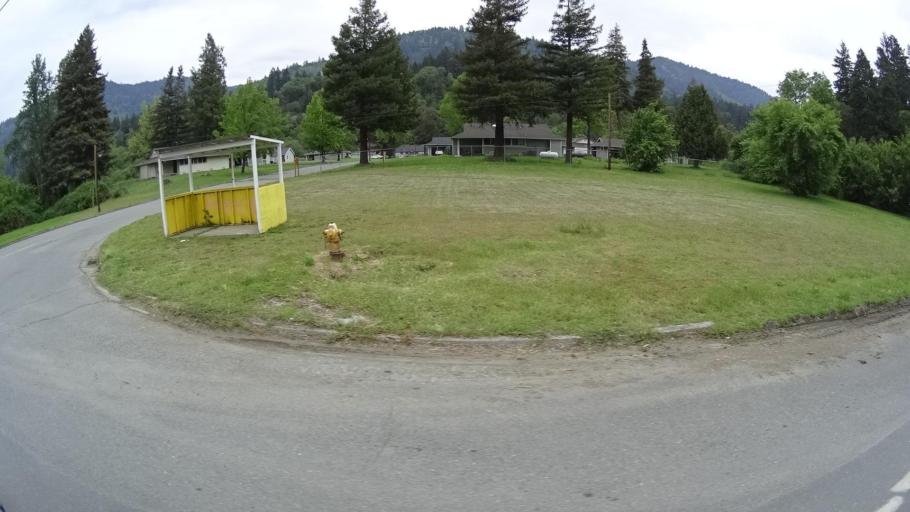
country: US
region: California
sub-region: Humboldt County
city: Willow Creek
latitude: 41.0677
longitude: -123.6866
